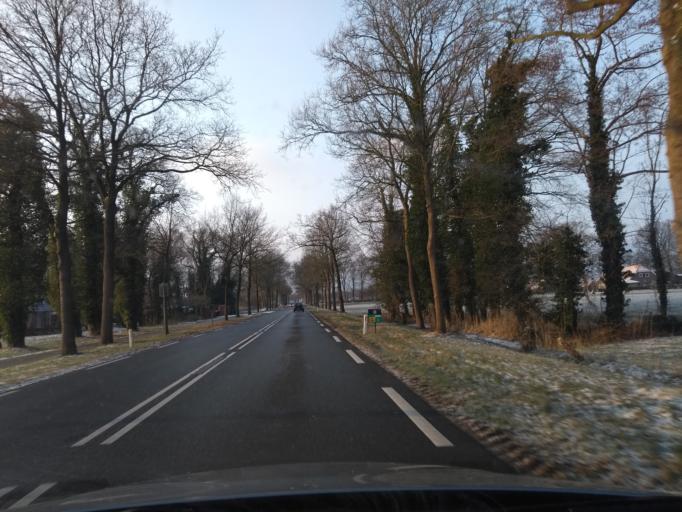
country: NL
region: Overijssel
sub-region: Gemeente Hof van Twente
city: Delden
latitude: 52.2433
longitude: 6.6941
